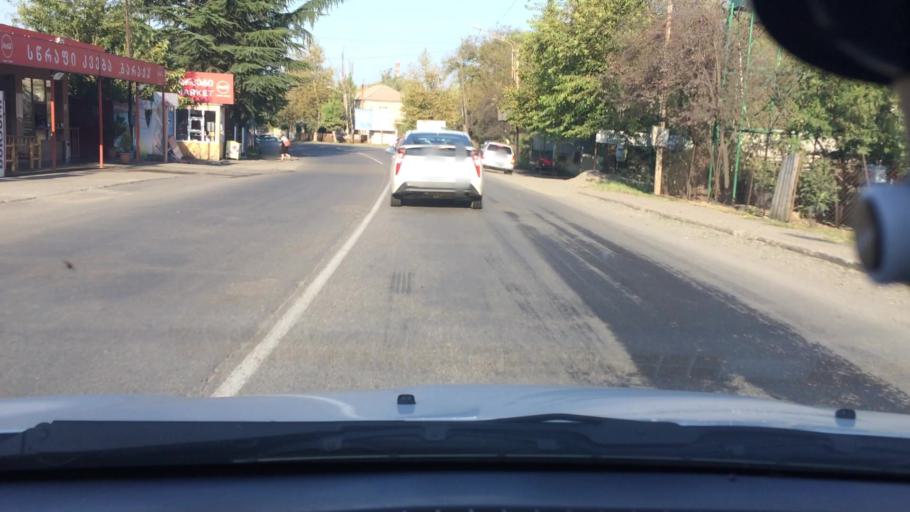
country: GE
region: Imereti
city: Zestap'oni
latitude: 42.1137
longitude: 43.0347
